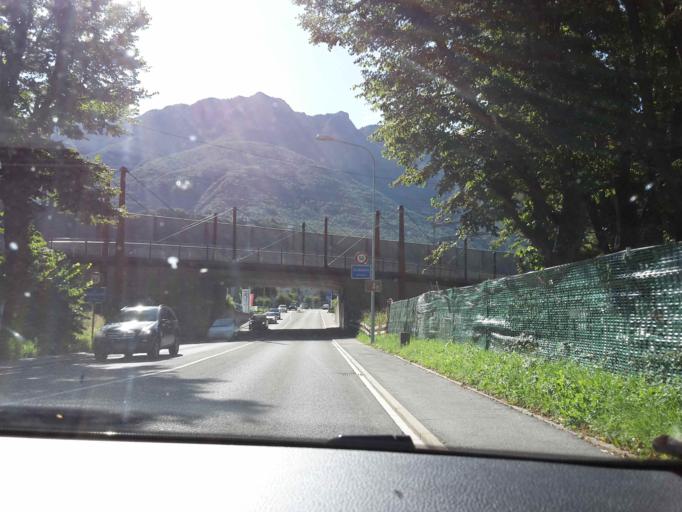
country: CH
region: Ticino
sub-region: Bellinzona District
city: Giubiasco
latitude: 46.1810
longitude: 9.0136
